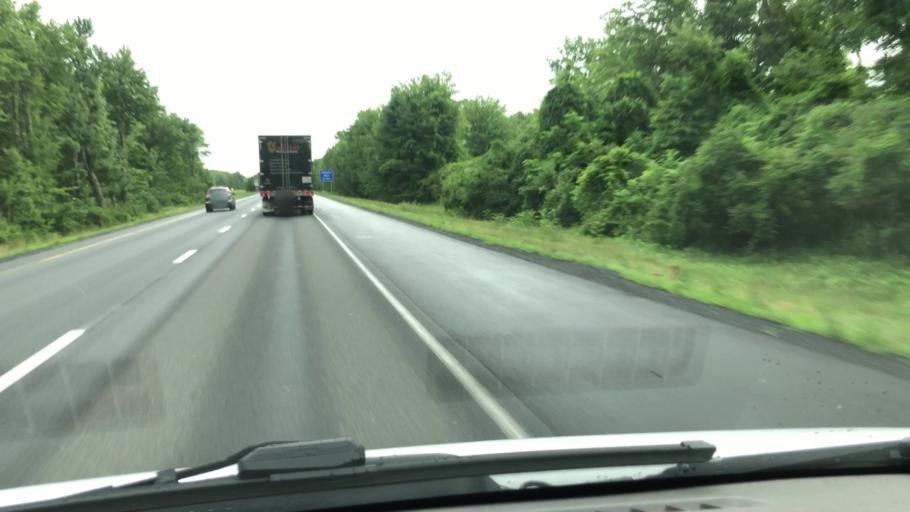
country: US
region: Massachusetts
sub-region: Franklin County
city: Whately
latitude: 42.4458
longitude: -72.6193
